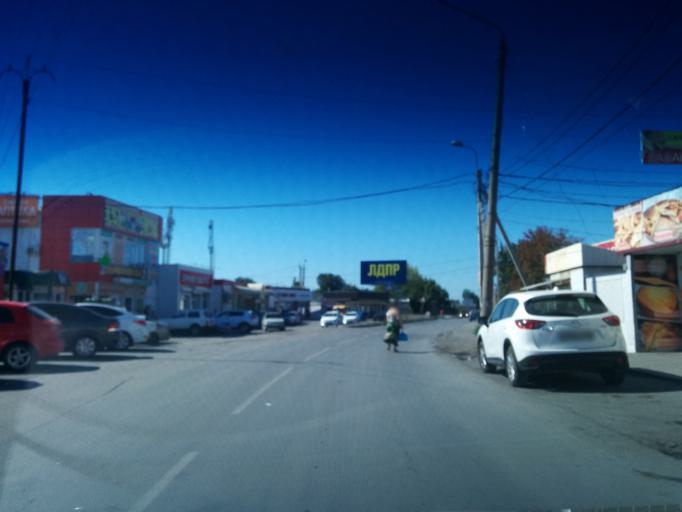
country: RU
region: Rostov
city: Shakhty
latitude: 47.6867
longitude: 40.2668
